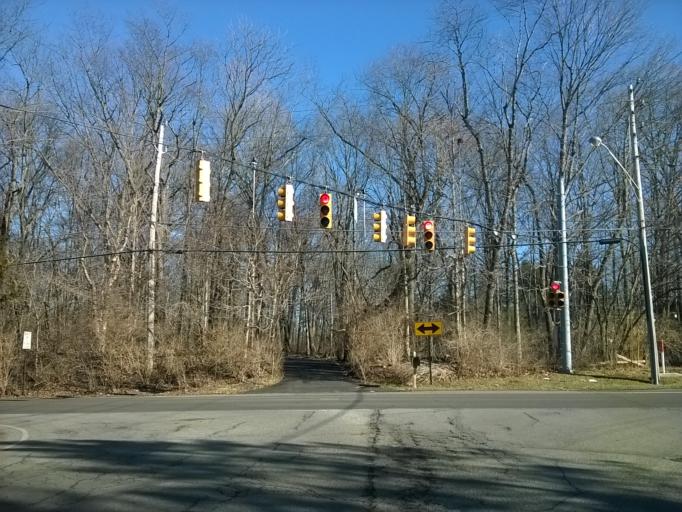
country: US
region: Indiana
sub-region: Marion County
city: Meridian Hills
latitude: 39.8976
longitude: -86.1653
